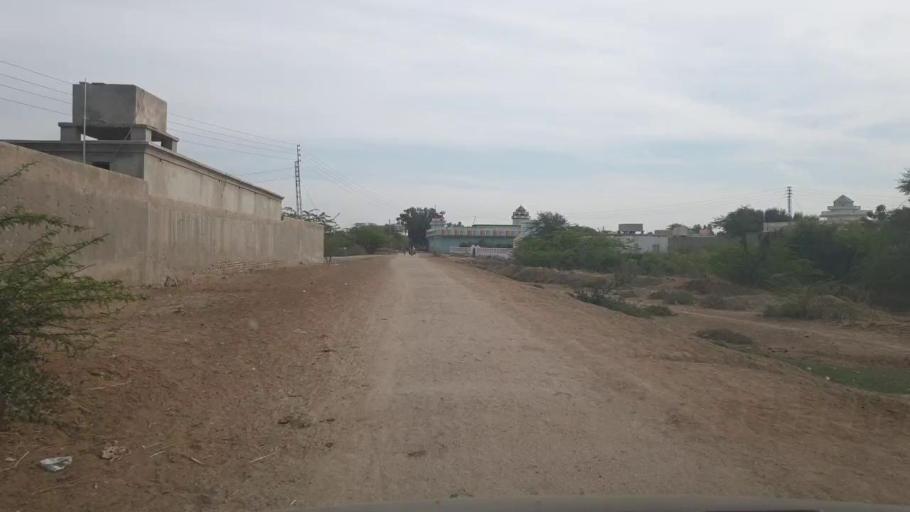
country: PK
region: Sindh
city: Kunri
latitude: 25.2854
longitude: 69.5984
